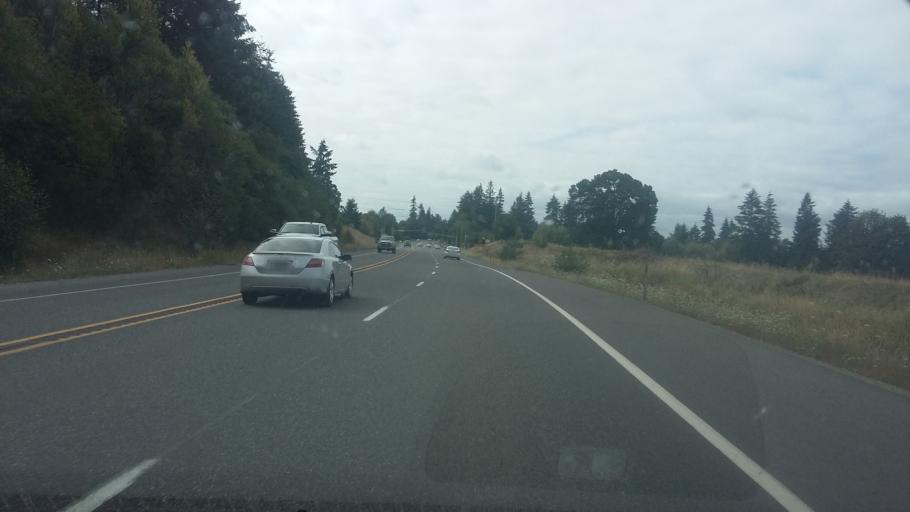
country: US
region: Washington
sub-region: Clark County
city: Battle Ground
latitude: 45.8022
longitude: -122.5494
